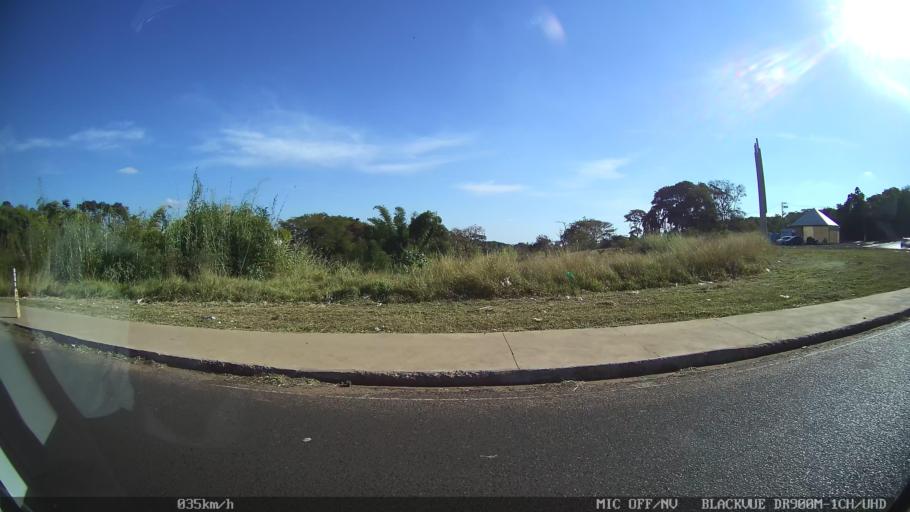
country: BR
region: Sao Paulo
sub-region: Franca
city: Franca
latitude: -20.5173
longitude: -47.4383
